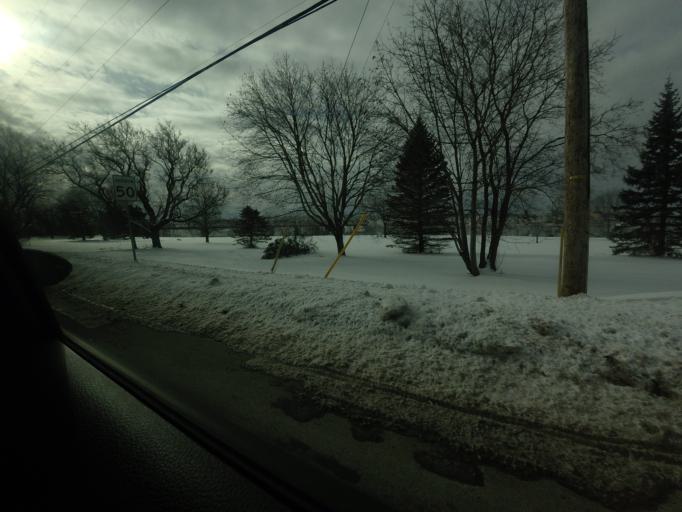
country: CA
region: New Brunswick
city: Fredericton
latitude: 45.9615
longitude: -66.6251
